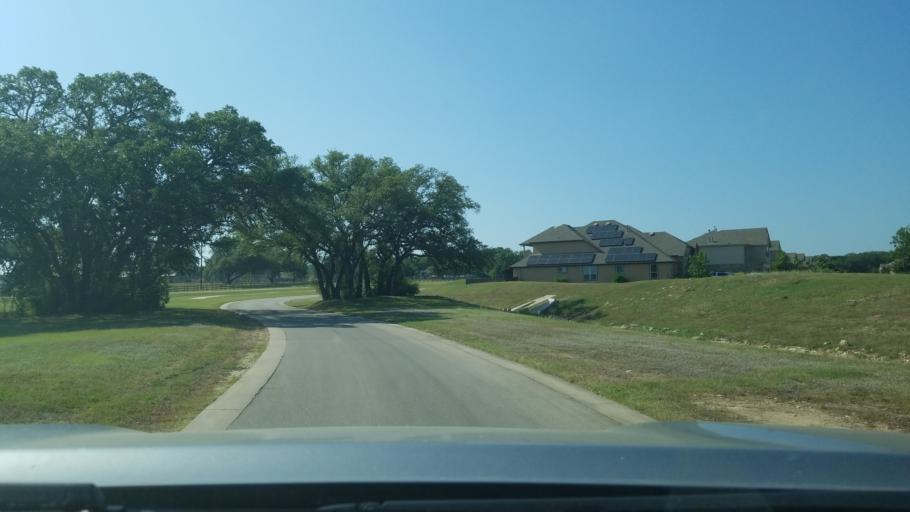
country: US
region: Texas
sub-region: Comal County
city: Bulverde
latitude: 29.7541
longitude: -98.4178
